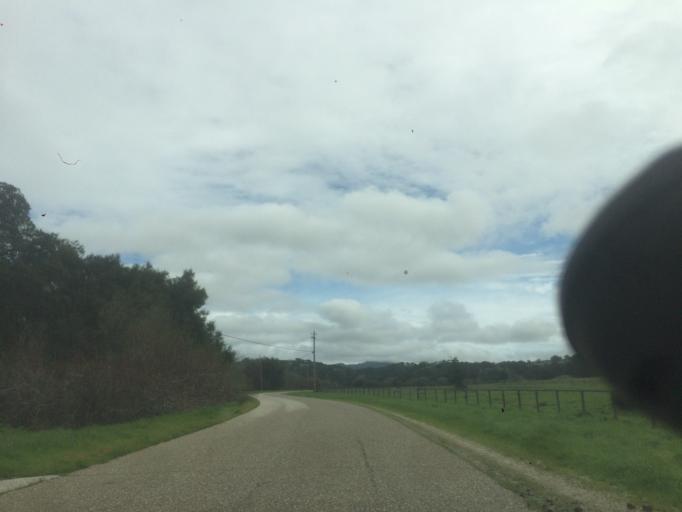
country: US
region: California
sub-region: San Luis Obispo County
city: Nipomo
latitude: 35.2062
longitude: -120.3979
